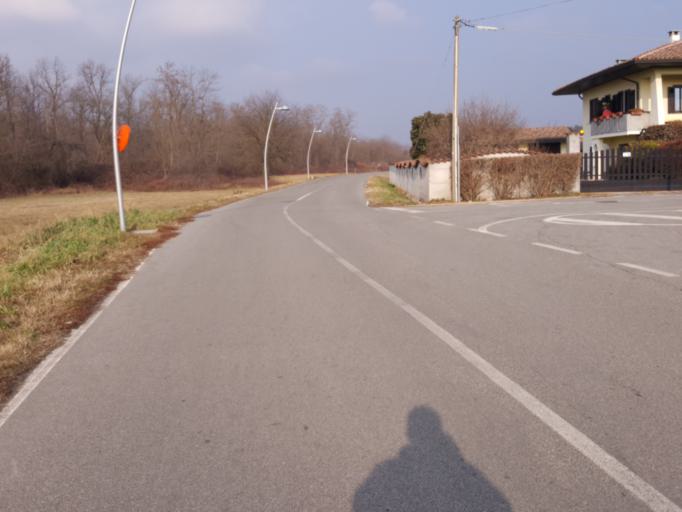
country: IT
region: Piedmont
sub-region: Provincia di Novara
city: Cressa
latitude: 45.6477
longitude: 8.5053
